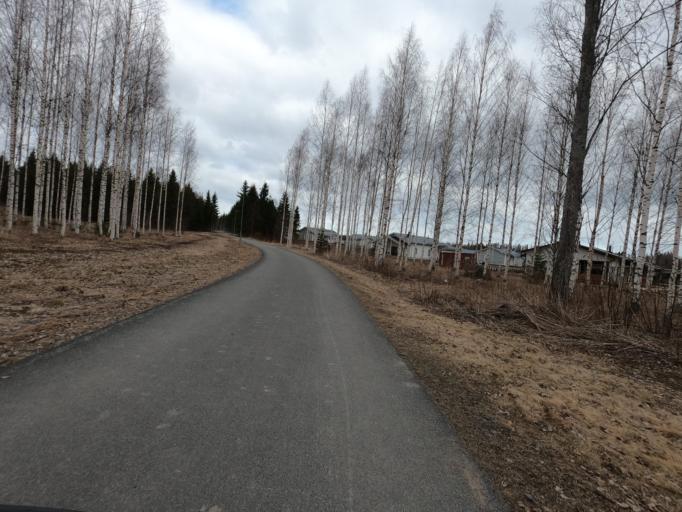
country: FI
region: North Karelia
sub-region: Joensuu
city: Joensuu
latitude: 62.5616
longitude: 29.8221
